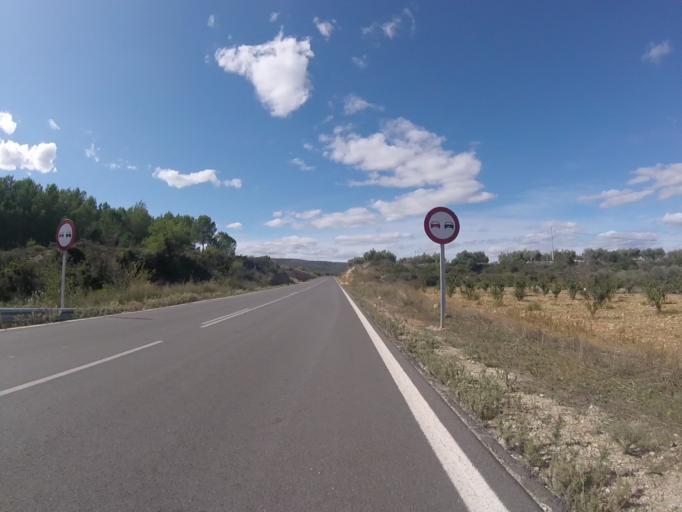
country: ES
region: Valencia
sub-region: Provincia de Castello
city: Chert/Xert
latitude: 40.4270
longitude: 0.1518
